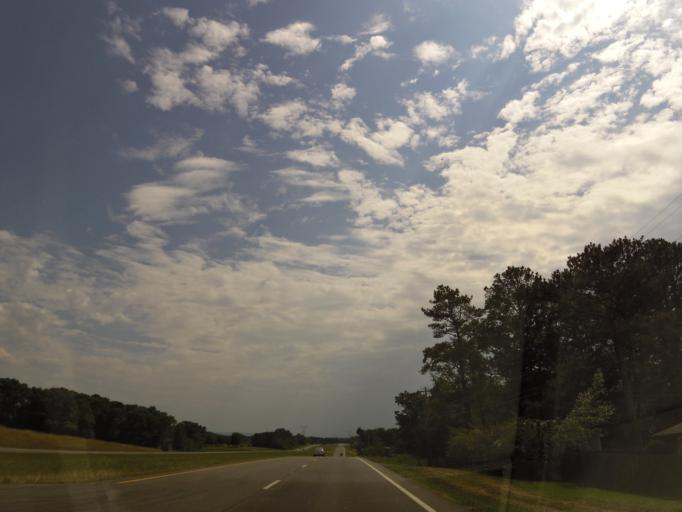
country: US
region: Alabama
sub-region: Jackson County
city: Stevenson
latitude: 34.7821
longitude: -85.8879
